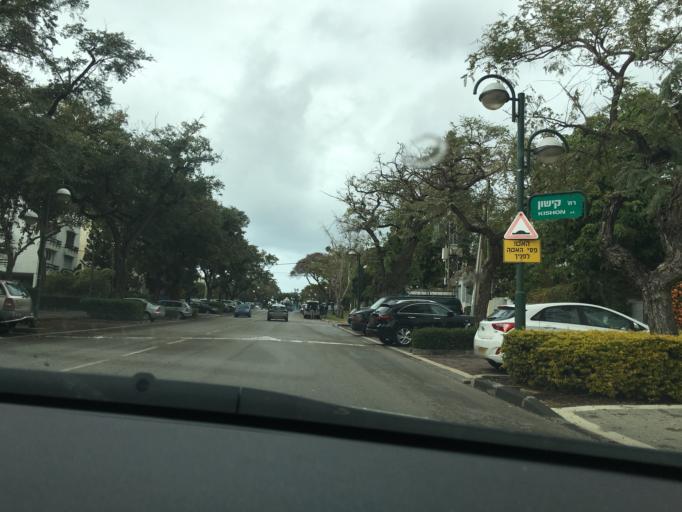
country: IL
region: Tel Aviv
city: Ramat HaSharon
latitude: 32.1433
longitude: 34.8468
